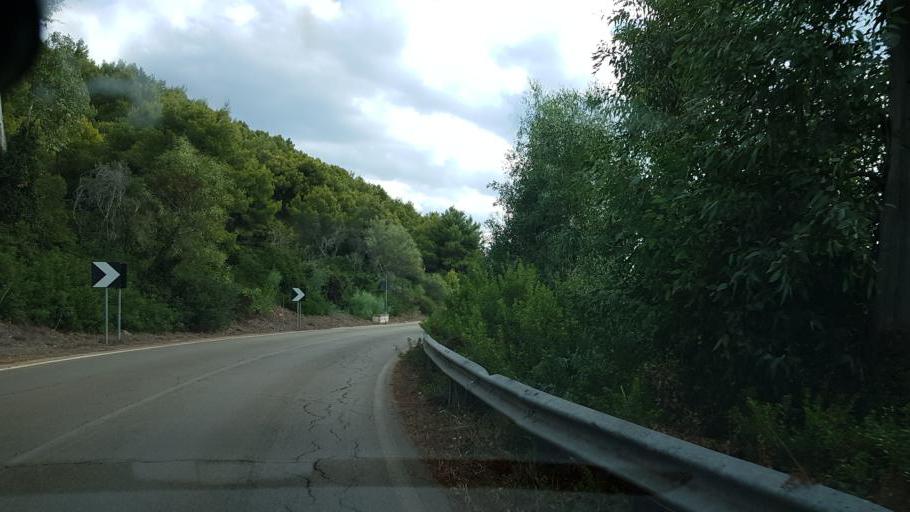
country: IT
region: Apulia
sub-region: Provincia di Lecce
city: Nardo
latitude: 40.1673
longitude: 17.9516
